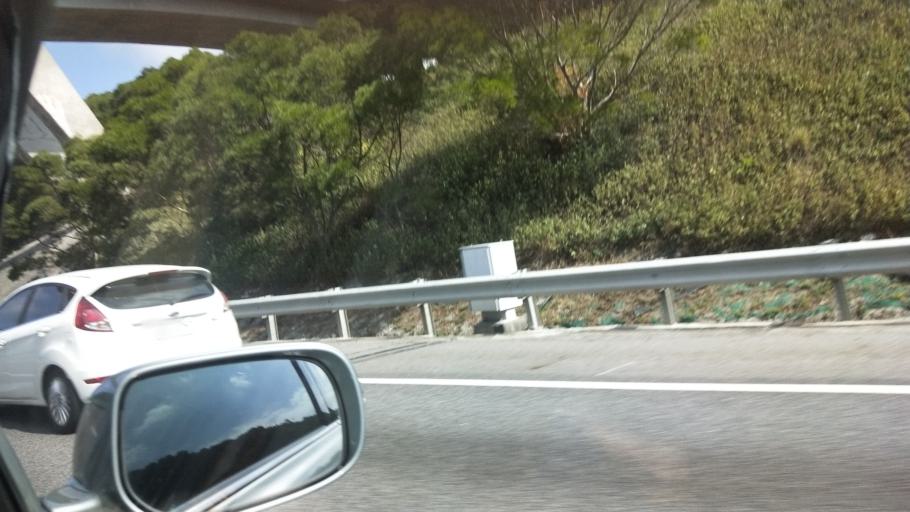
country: TW
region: Taiwan
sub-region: Miaoli
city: Miaoli
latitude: 24.4513
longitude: 120.6786
